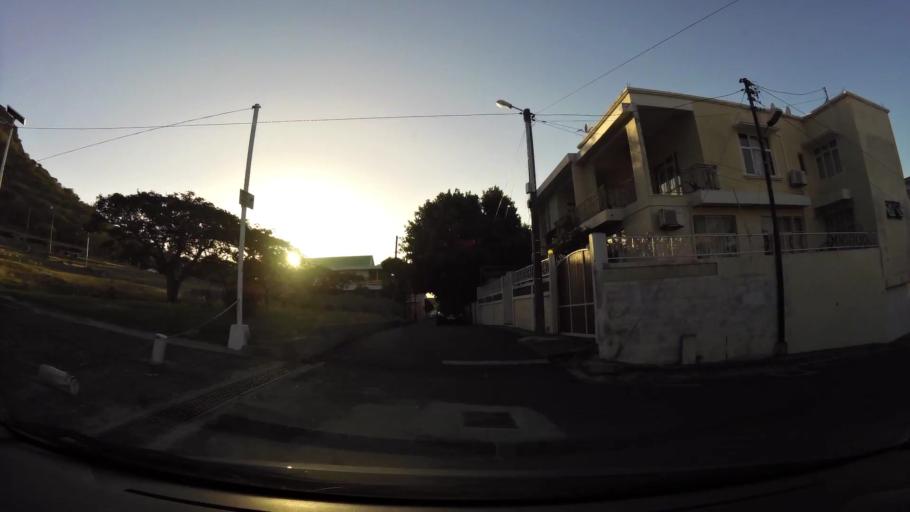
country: MU
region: Port Louis
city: Port Louis
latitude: -20.1695
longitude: 57.4973
